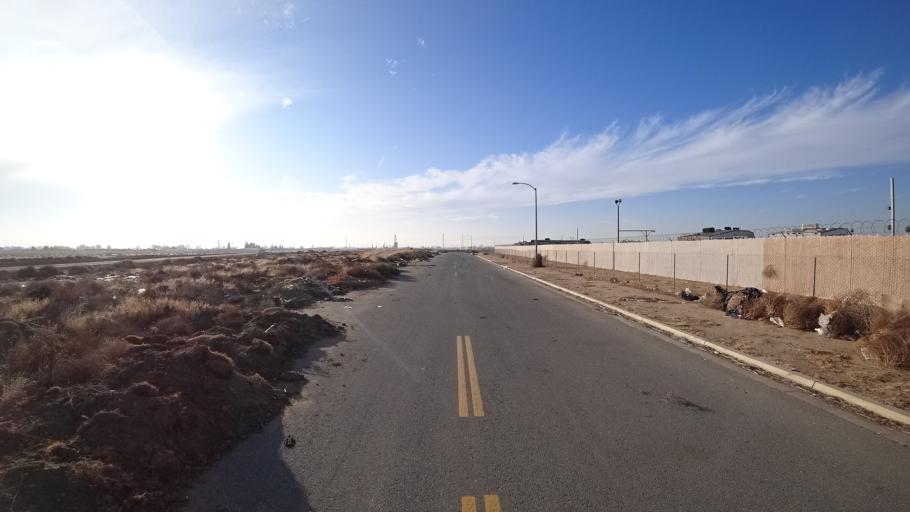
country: US
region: California
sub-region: Kern County
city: Oildale
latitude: 35.4077
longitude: -119.0567
